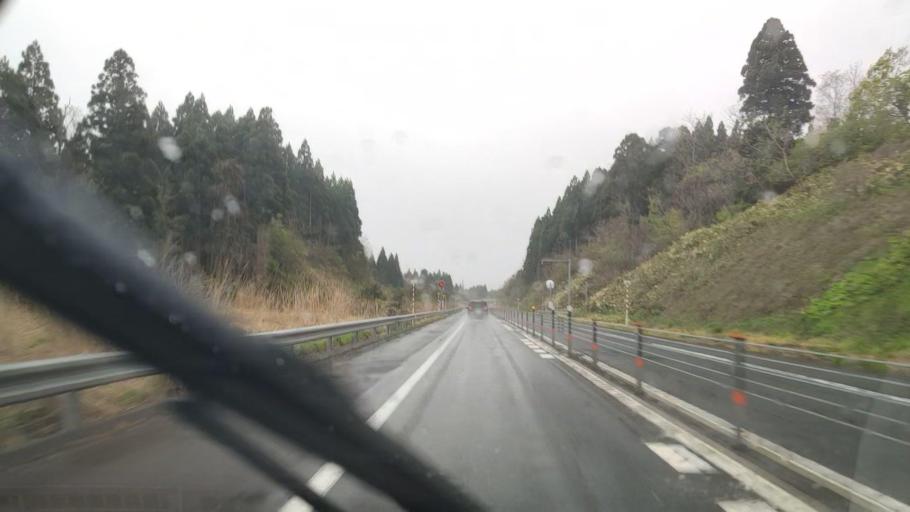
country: JP
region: Akita
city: Noshiromachi
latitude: 40.1734
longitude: 140.0547
